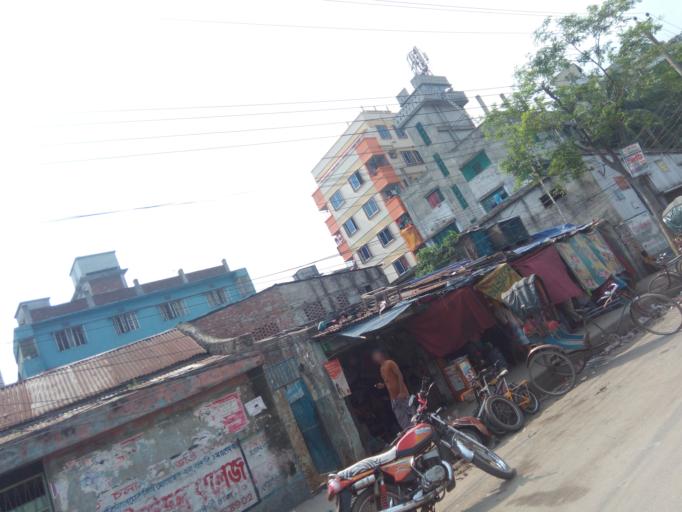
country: BD
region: Dhaka
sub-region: Dhaka
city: Dhaka
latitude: 23.7063
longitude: 90.4197
